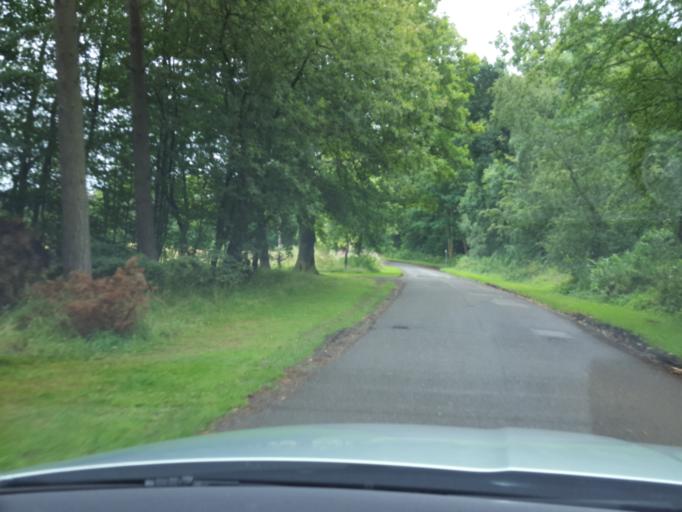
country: GB
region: Scotland
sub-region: Falkirk
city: Polmont
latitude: 55.9621
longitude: -3.6666
